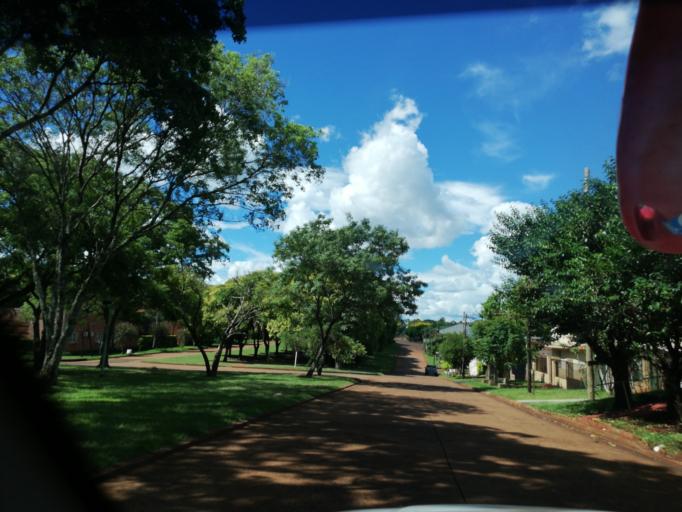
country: AR
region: Misiones
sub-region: Departamento de Apostoles
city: Apostoles
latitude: -27.9122
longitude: -55.7453
